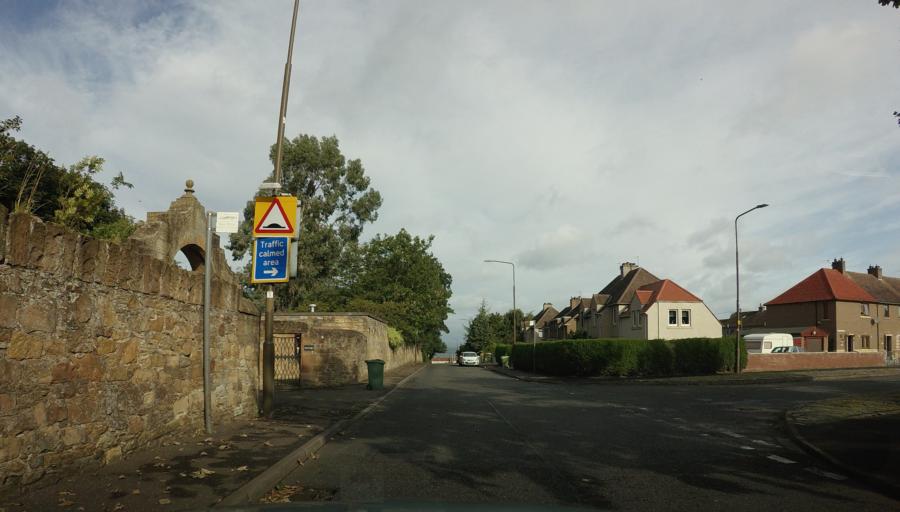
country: GB
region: Scotland
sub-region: East Lothian
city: Prestonpans
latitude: 55.9538
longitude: -2.9930
